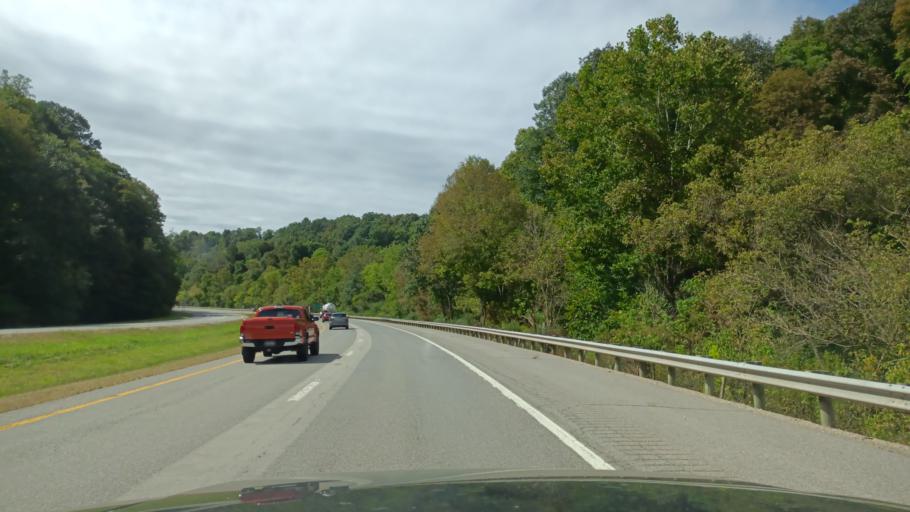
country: US
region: West Virginia
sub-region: Pleasants County
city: Saint Marys
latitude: 39.2561
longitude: -81.1902
